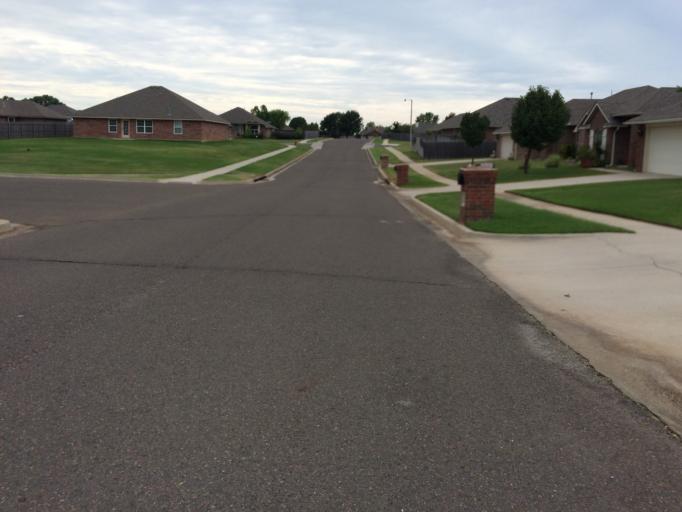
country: US
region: Oklahoma
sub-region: Cleveland County
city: Hall Park
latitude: 35.2437
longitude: -97.4189
